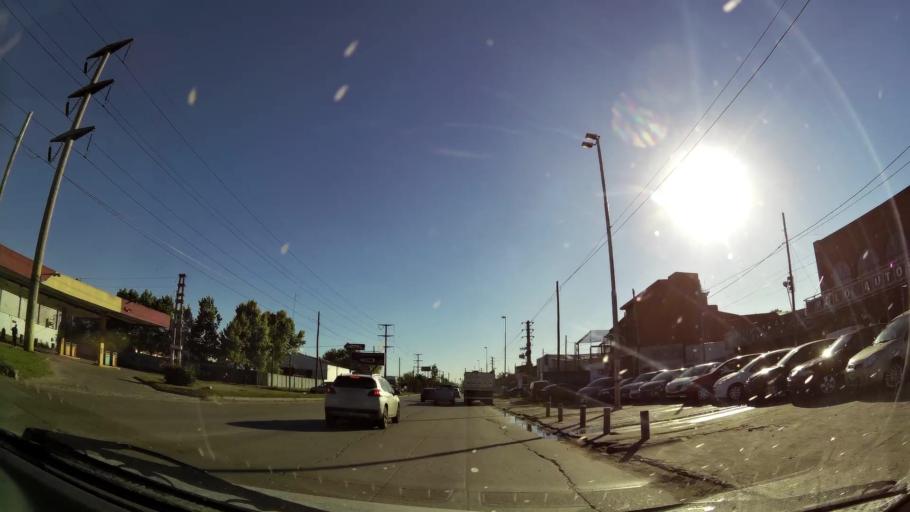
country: AR
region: Buenos Aires
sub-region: Partido de Quilmes
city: Quilmes
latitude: -34.7437
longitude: -58.3265
